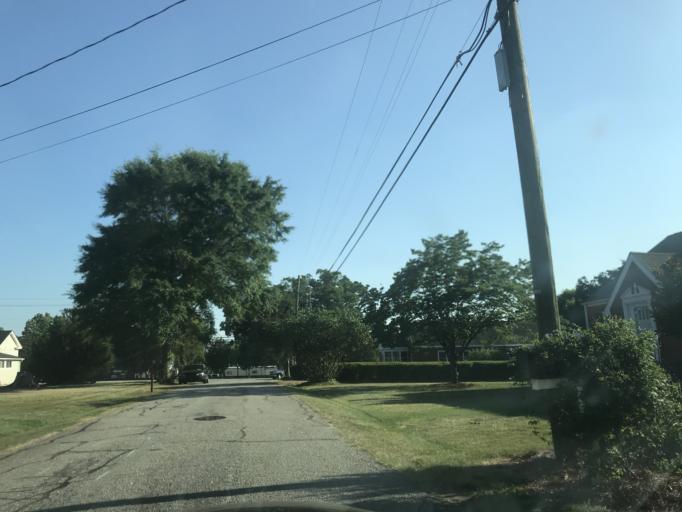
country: US
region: North Carolina
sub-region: Wake County
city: Garner
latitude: 35.7084
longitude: -78.6061
